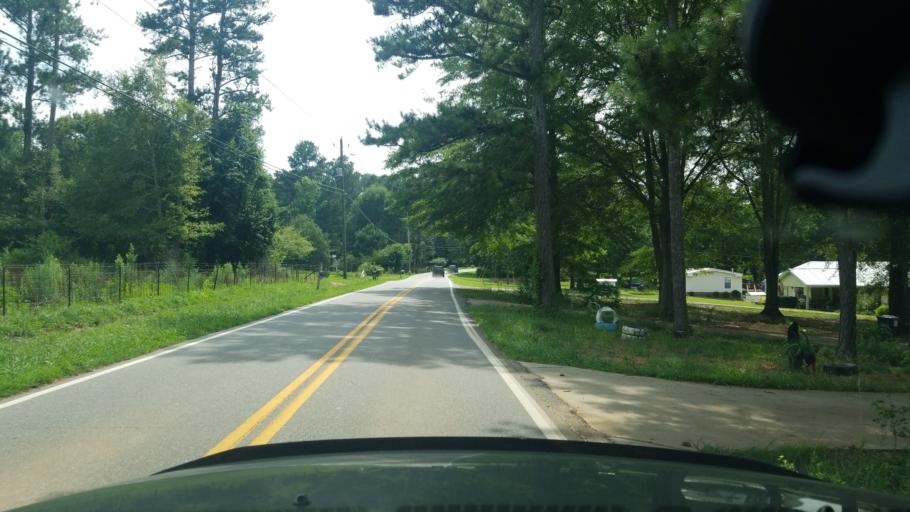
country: US
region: Georgia
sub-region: Forsyth County
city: Cumming
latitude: 34.2710
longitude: -84.1693
